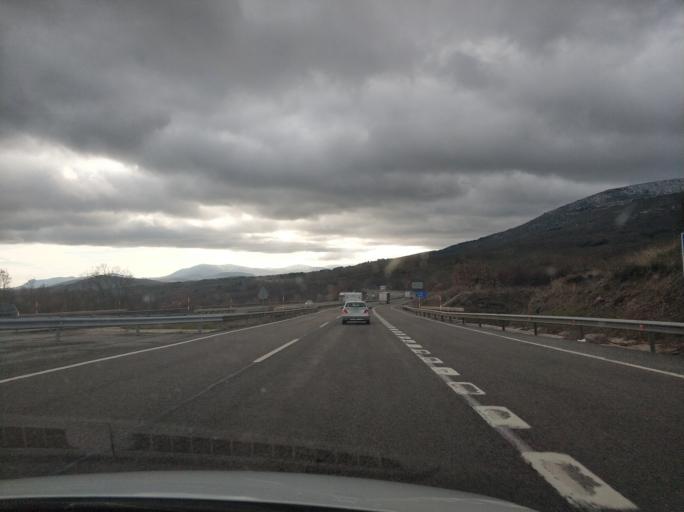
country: ES
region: Madrid
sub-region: Provincia de Madrid
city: Horcajo de la Sierra
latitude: 41.0805
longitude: -3.5996
